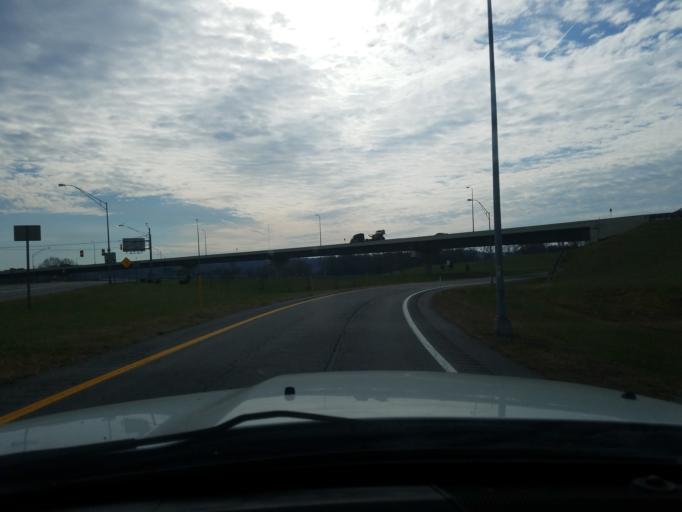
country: US
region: West Virginia
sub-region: Putnam County
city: Teays Valley
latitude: 38.4561
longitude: -81.9044
